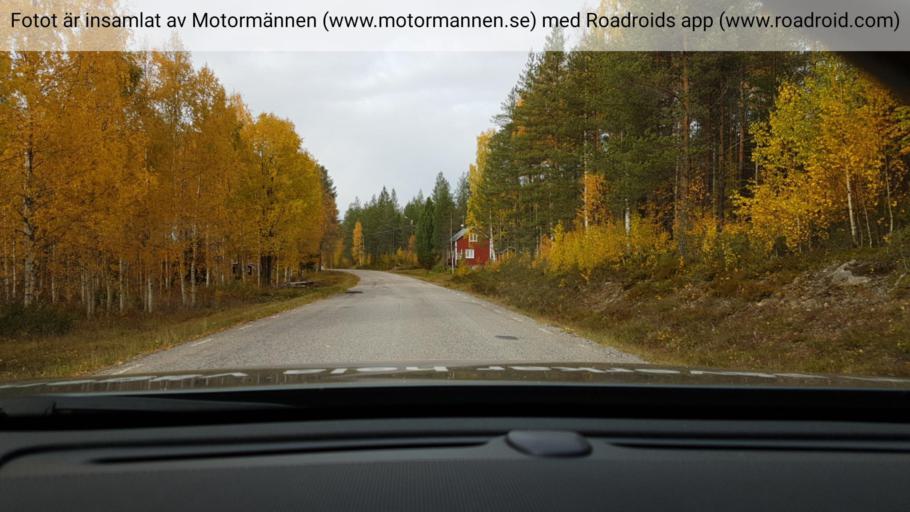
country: SE
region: Norrbotten
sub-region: Overkalix Kommun
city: OEverkalix
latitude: 66.2545
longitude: 23.1220
